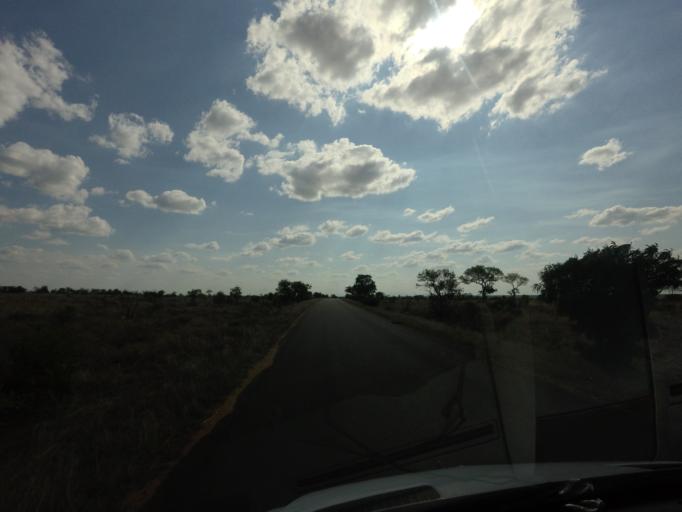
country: ZA
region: Limpopo
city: Thulamahashi
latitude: -24.3921
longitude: 31.6054
